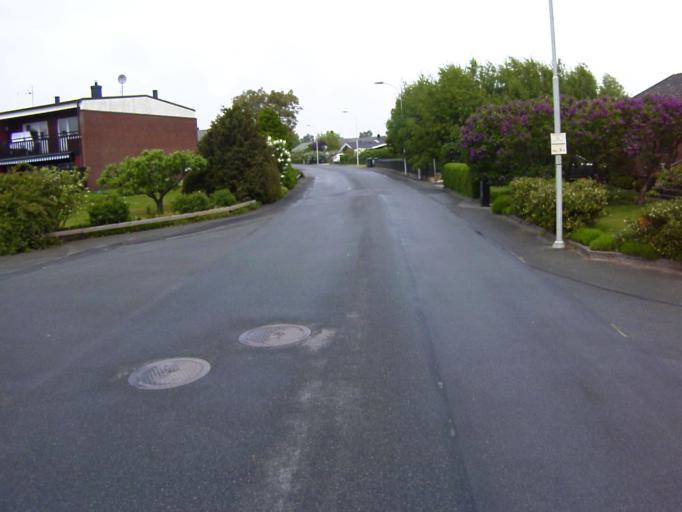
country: SE
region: Skane
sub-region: Kristianstads Kommun
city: Ahus
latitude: 55.9241
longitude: 14.2870
